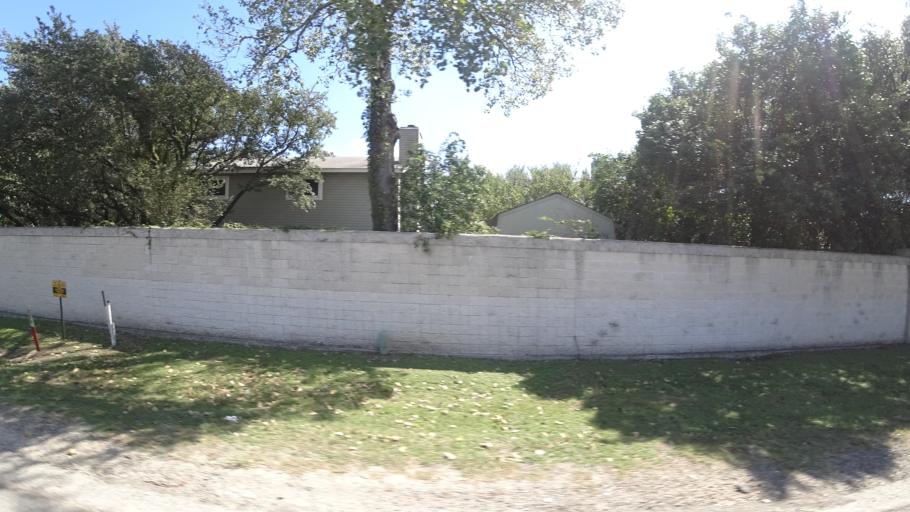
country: US
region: Texas
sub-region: Williamson County
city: Anderson Mill
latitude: 30.4589
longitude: -97.8221
